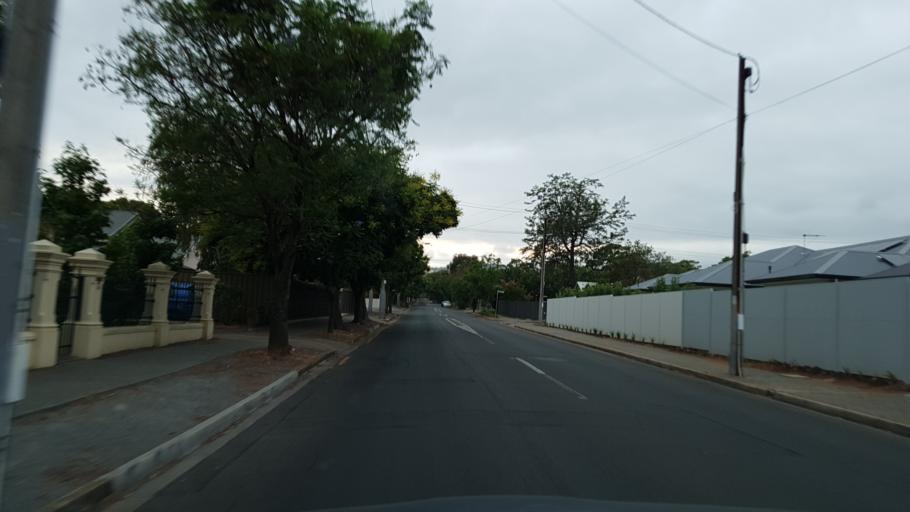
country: AU
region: South Australia
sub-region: Mitcham
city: Hawthorn
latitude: -34.9765
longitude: 138.6015
